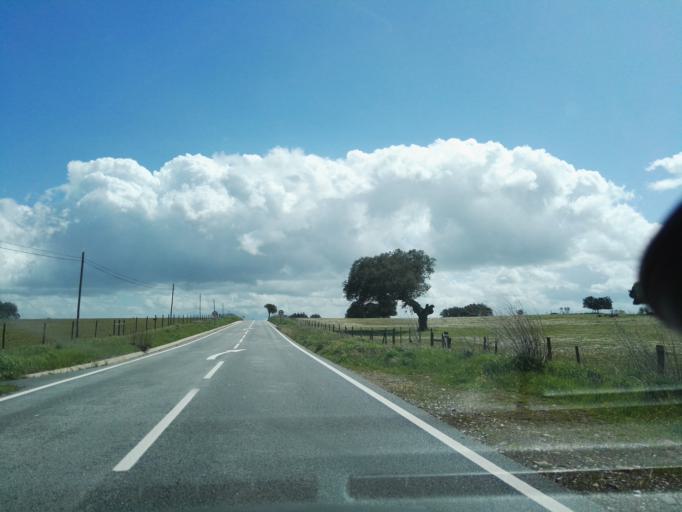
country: PT
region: Portalegre
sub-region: Arronches
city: Arronches
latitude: 39.1202
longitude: -7.2668
